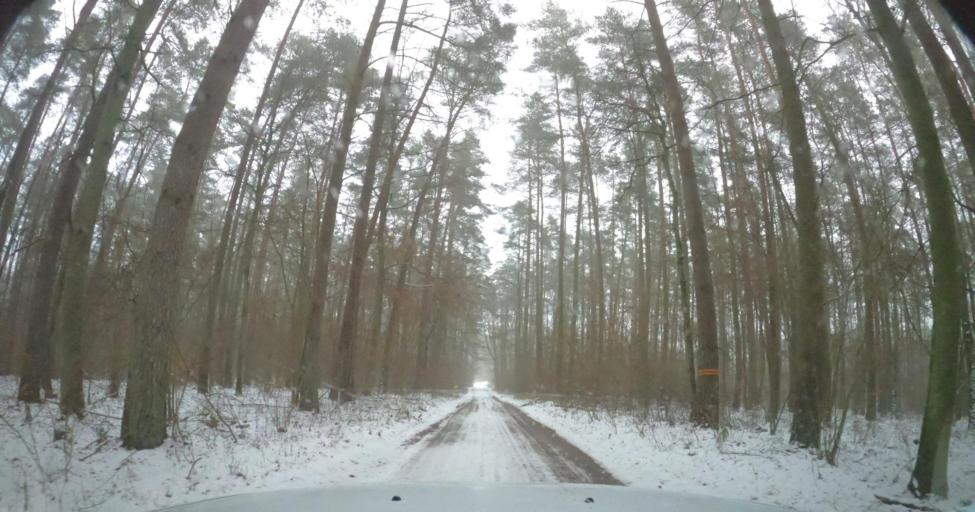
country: PL
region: West Pomeranian Voivodeship
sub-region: Powiat kamienski
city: Golczewo
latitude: 53.7700
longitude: 14.9313
